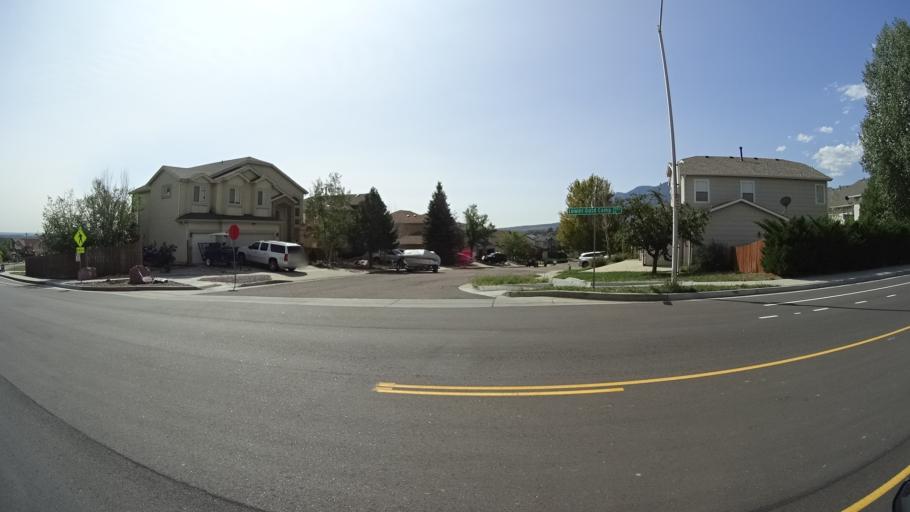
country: US
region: Colorado
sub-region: El Paso County
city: Colorado Springs
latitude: 38.8283
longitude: -104.8550
